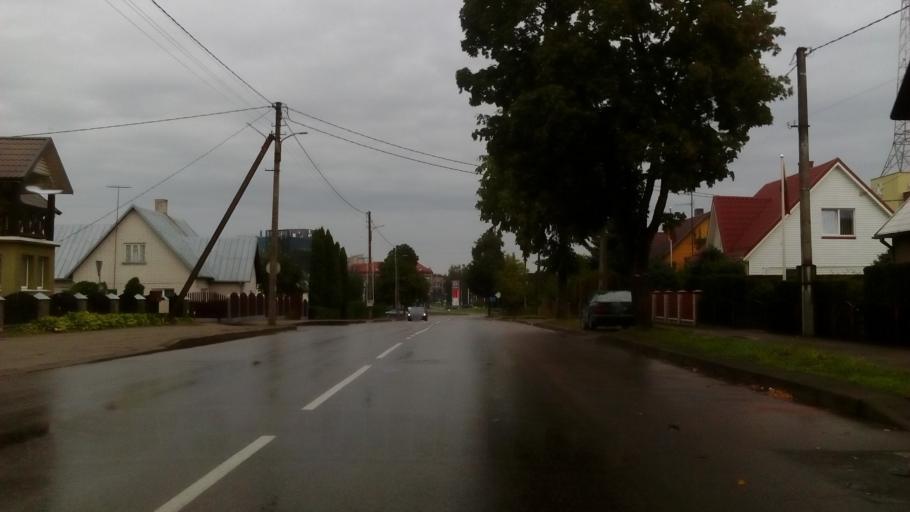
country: LT
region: Alytaus apskritis
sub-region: Alytus
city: Alytus
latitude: 54.3925
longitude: 24.0391
